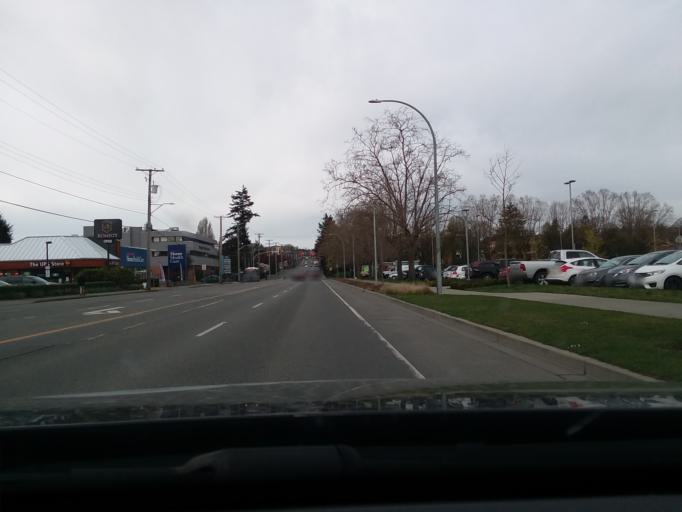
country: CA
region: British Columbia
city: Oak Bay
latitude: 48.4445
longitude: -123.3364
